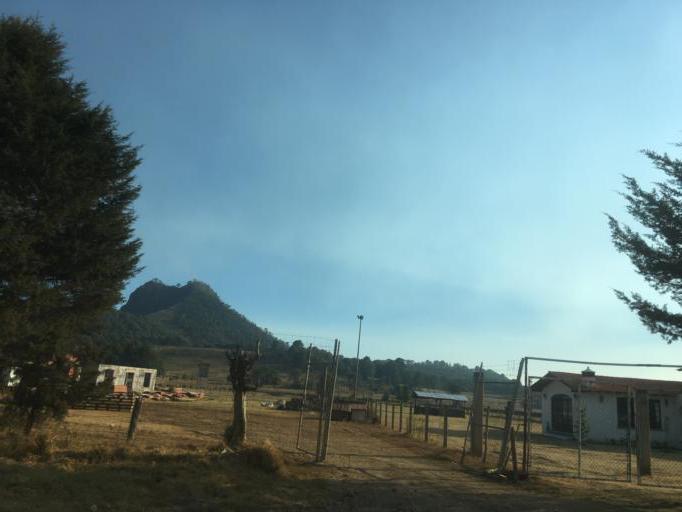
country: MX
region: Michoacan
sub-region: Morelia
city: Iratzio
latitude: 19.6302
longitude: -101.4664
